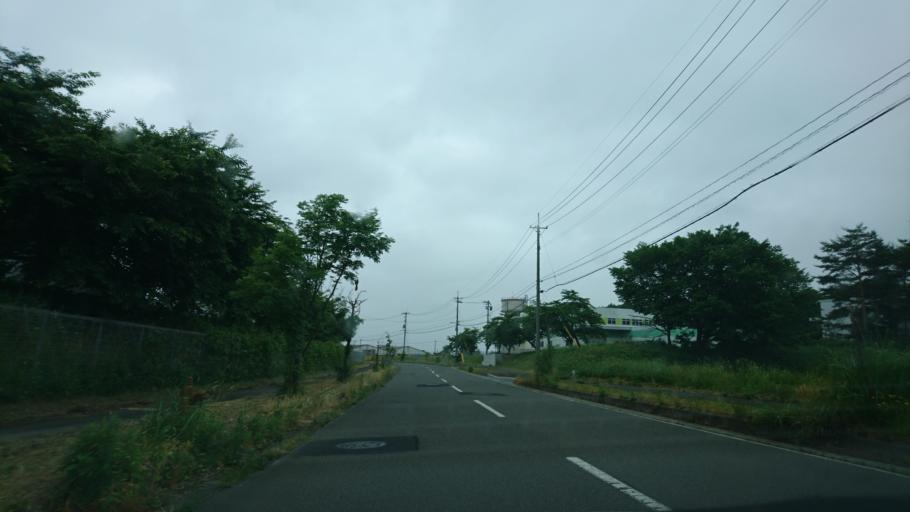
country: JP
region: Iwate
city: Ichinoseki
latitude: 38.9218
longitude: 141.1668
